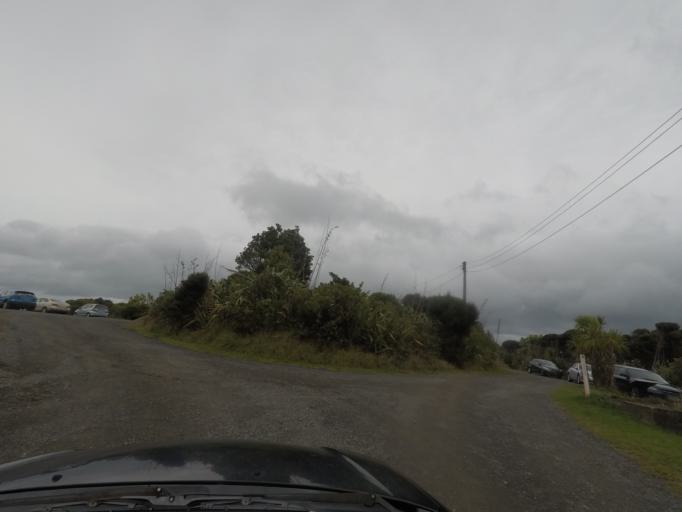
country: NZ
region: Auckland
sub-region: Auckland
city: Muriwai Beach
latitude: -36.9698
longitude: 174.4683
